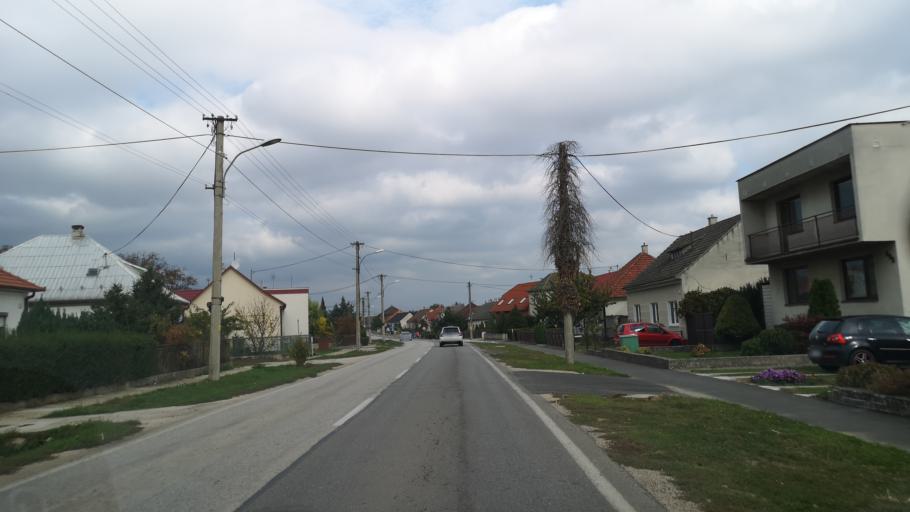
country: SK
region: Nitriansky
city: Cachtice
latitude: 48.6691
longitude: 17.7675
